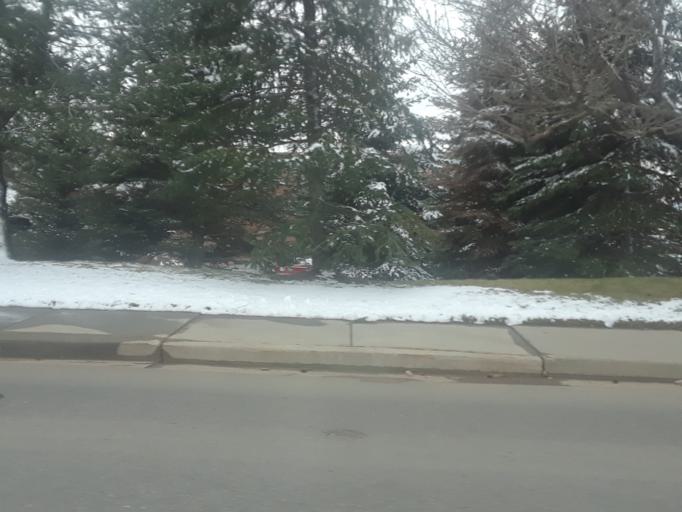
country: US
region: Colorado
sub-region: Arapahoe County
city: Centennial
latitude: 39.5749
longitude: -104.8816
